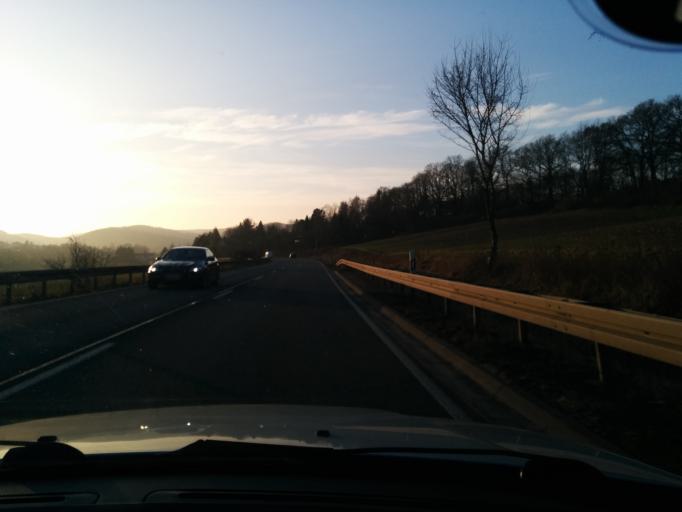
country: DE
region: Hesse
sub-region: Regierungsbezirk Kassel
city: Sontra
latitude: 51.1380
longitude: 9.9546
